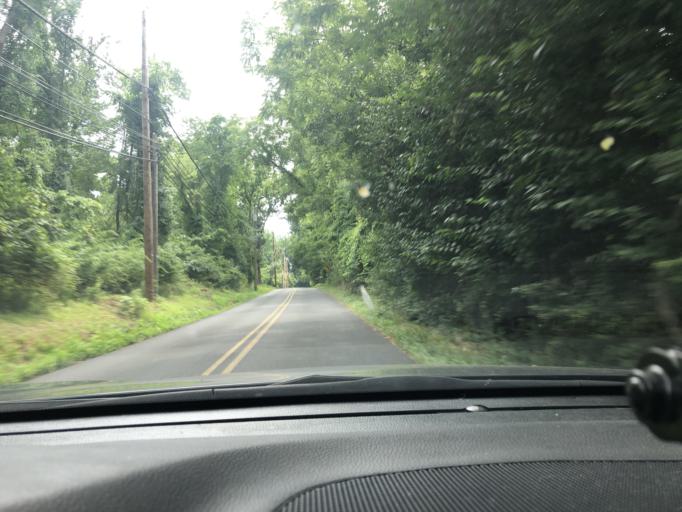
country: US
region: Pennsylvania
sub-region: Montgomery County
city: Blue Bell
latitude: 40.1519
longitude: -75.2495
